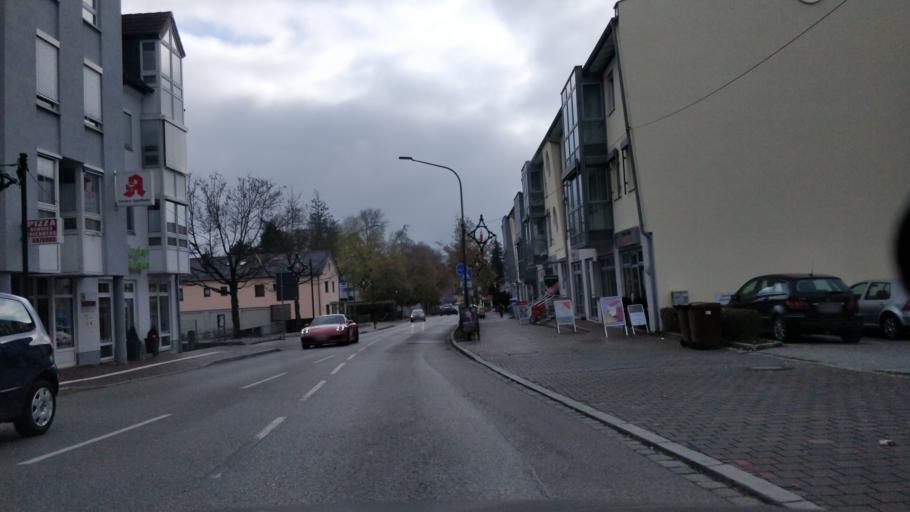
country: DE
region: Bavaria
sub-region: Swabia
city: Friedberg
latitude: 48.3552
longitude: 10.9843
